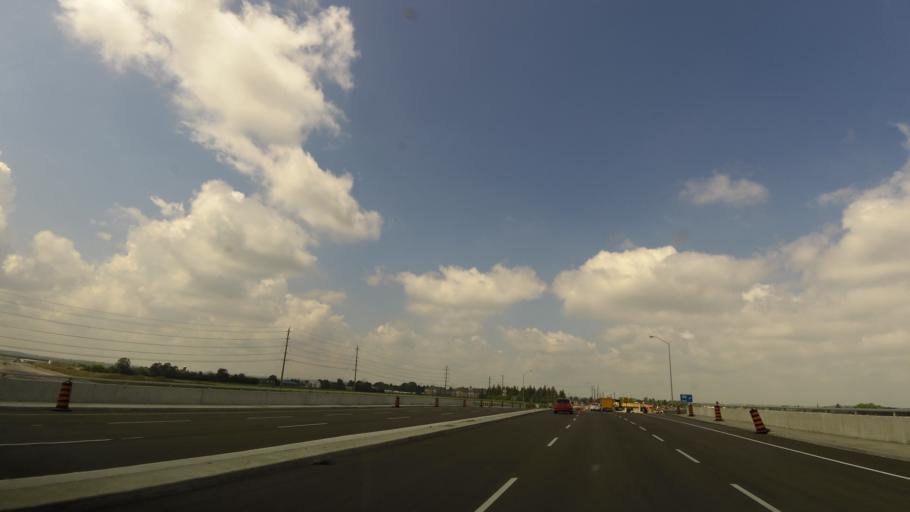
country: CA
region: Ontario
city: Oshawa
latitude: 43.9473
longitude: -78.9598
